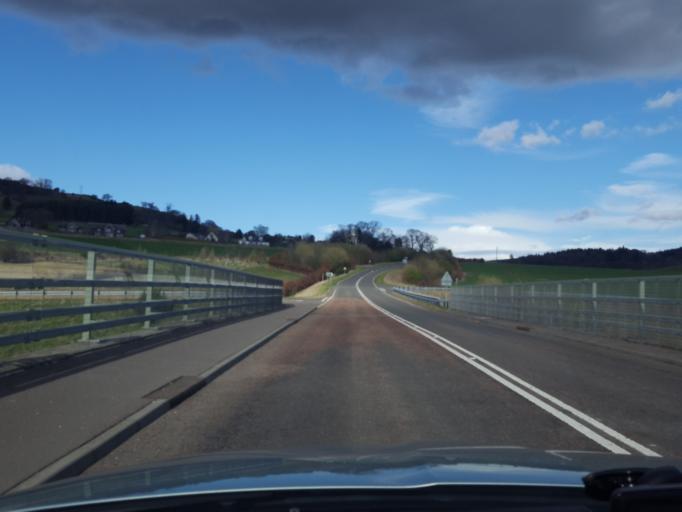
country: GB
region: Scotland
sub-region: Perth and Kinross
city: Abernethy
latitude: 56.3814
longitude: -3.3508
